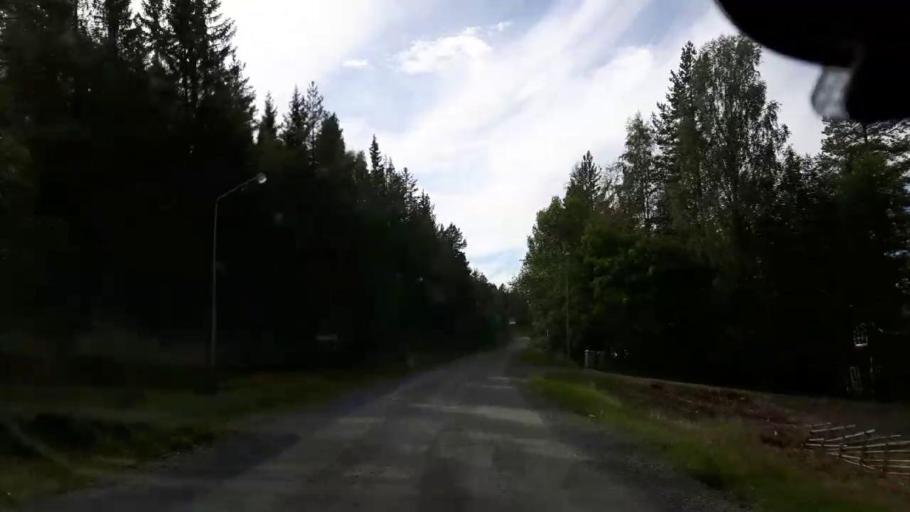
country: SE
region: Jaemtland
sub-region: Ragunda Kommun
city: Hammarstrand
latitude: 63.1386
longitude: 16.1929
